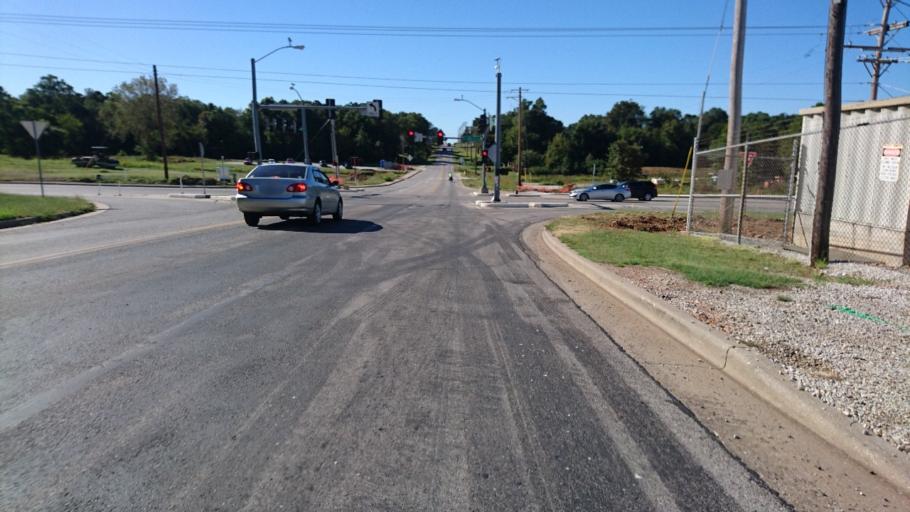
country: US
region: Missouri
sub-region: Jasper County
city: Joplin
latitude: 37.1136
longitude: -94.4940
